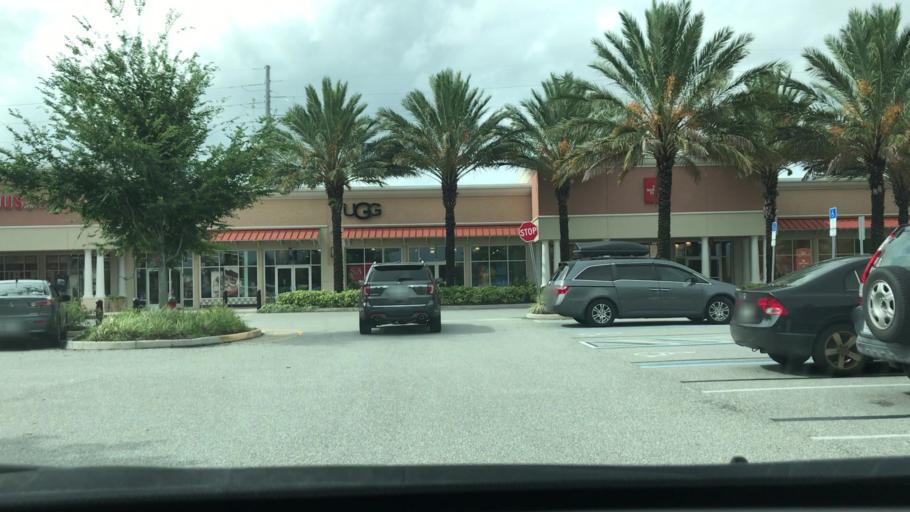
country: US
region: Florida
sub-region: Orange County
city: Williamsburg
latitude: 28.3904
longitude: -81.4907
